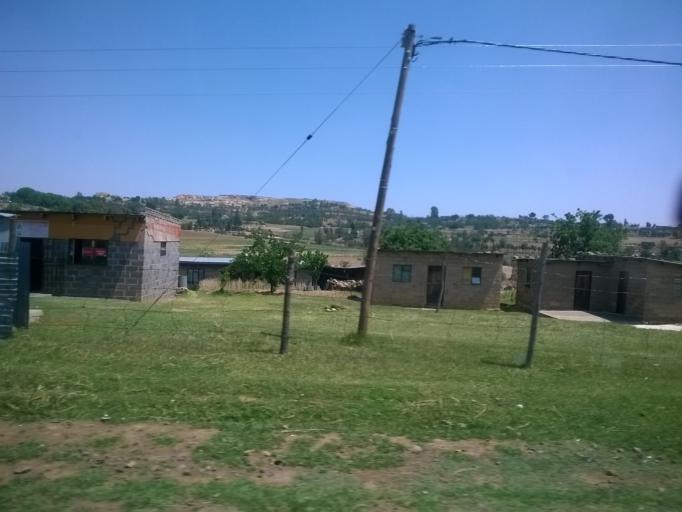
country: LS
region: Berea
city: Teyateyaneng
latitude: -29.1072
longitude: 27.8335
